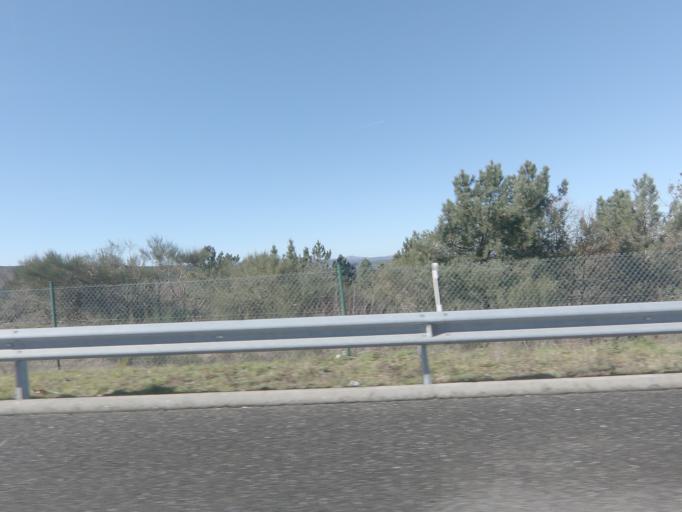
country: ES
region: Galicia
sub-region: Provincia de Pontevedra
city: Dozon
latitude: 42.5749
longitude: -8.0616
